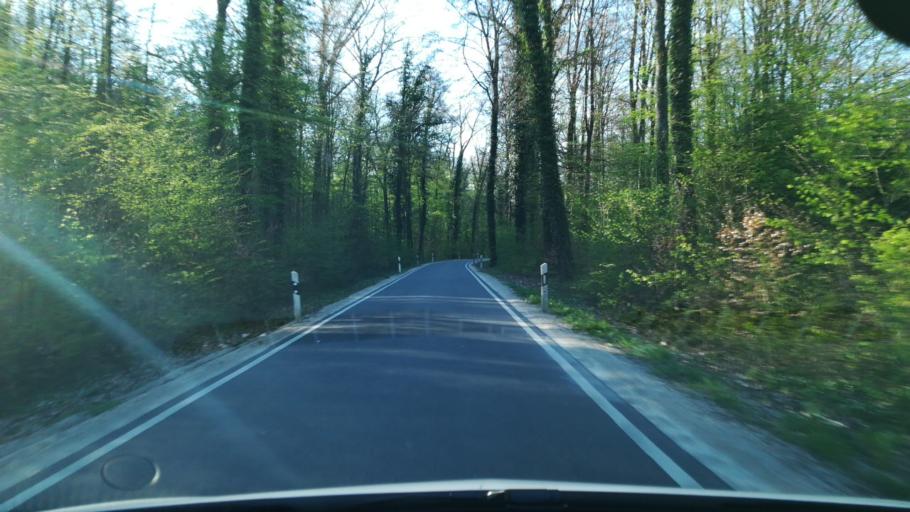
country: DE
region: Baden-Wuerttemberg
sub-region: Freiburg Region
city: Singen
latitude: 47.7725
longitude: 8.8551
